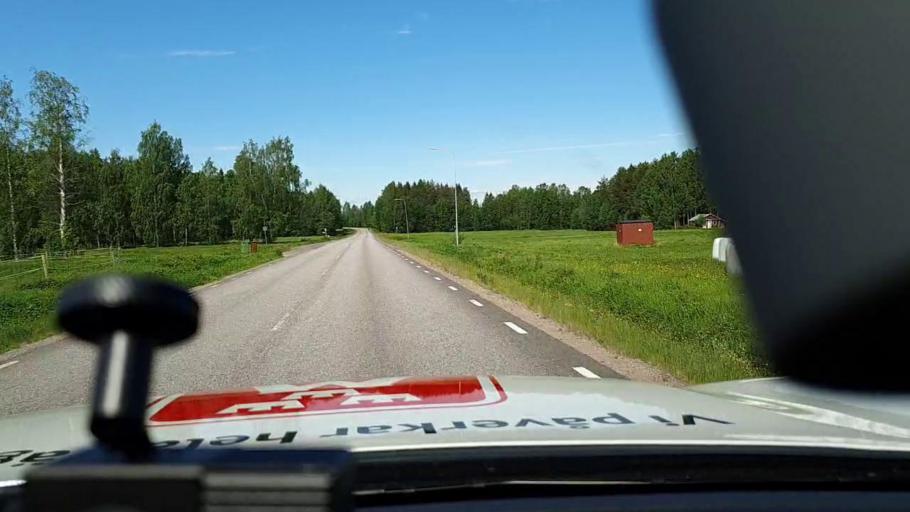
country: SE
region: Norrbotten
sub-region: Lulea Kommun
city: Sodra Sunderbyn
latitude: 65.6569
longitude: 21.8457
